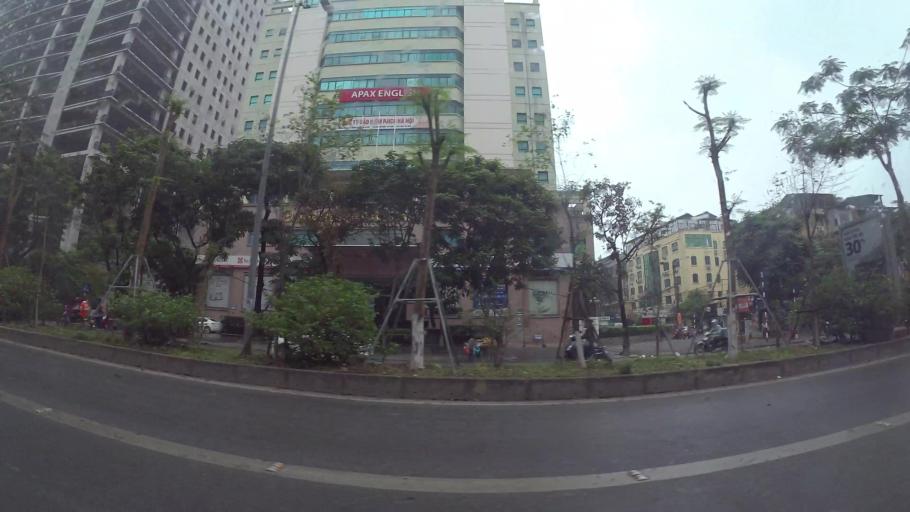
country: VN
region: Ha Noi
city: Dong Da
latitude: 21.0193
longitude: 105.8170
